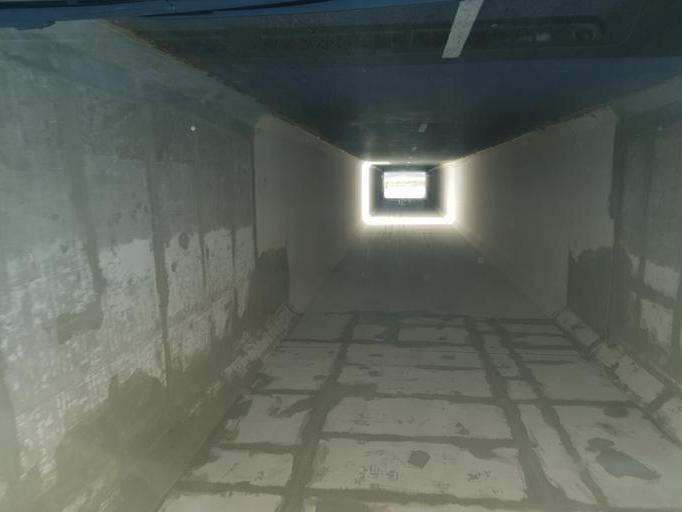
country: AE
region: Ash Shariqah
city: Sharjah
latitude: 25.2868
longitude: 55.5892
